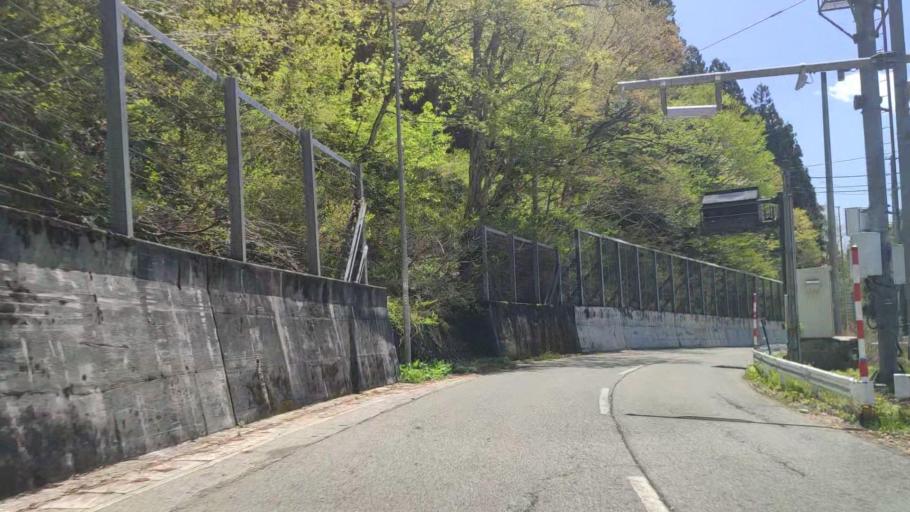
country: JP
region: Yamagata
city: Shinjo
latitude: 38.9587
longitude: 140.3585
